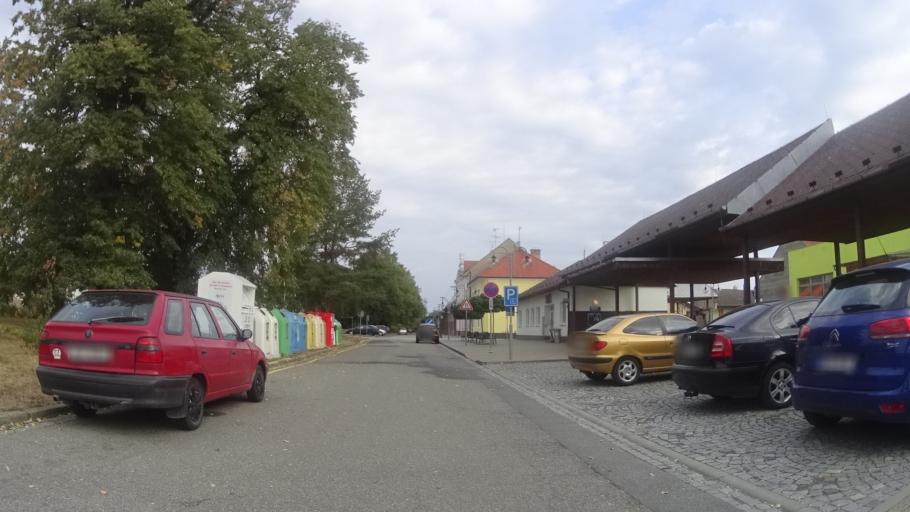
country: CZ
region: Zlin
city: Chropyne
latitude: 49.3574
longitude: 17.3637
